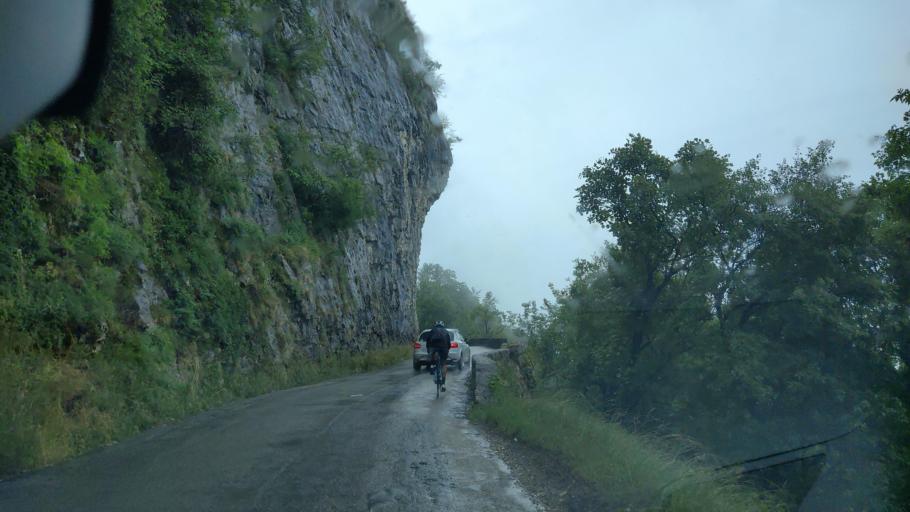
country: FR
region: Rhone-Alpes
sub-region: Departement de la Savoie
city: Chatillon
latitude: 45.7770
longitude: 5.8725
